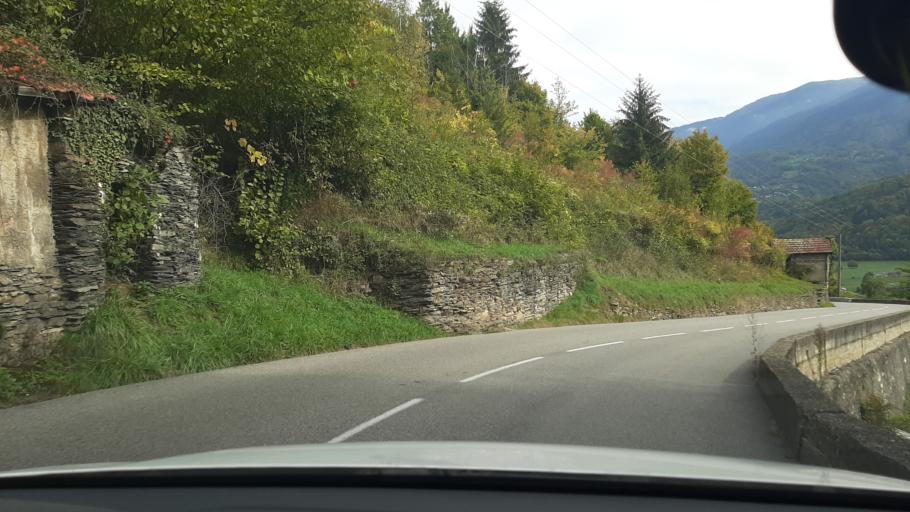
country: FR
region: Rhone-Alpes
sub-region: Departement de la Savoie
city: La Rochette
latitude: 45.4479
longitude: 6.0886
